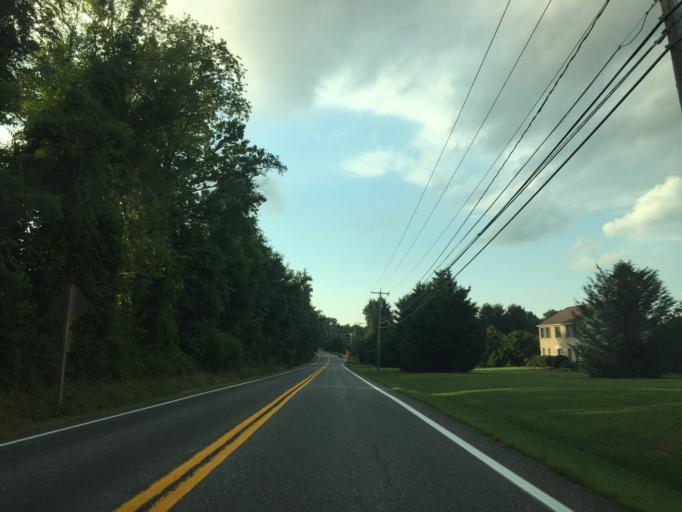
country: US
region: Maryland
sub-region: Harford County
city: Jarrettsville
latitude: 39.5772
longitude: -76.5001
